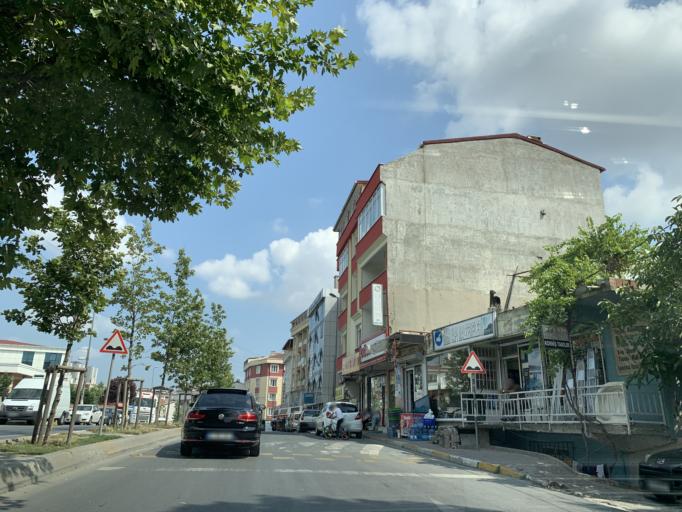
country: TR
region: Istanbul
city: Esenyurt
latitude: 41.0387
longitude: 28.6632
